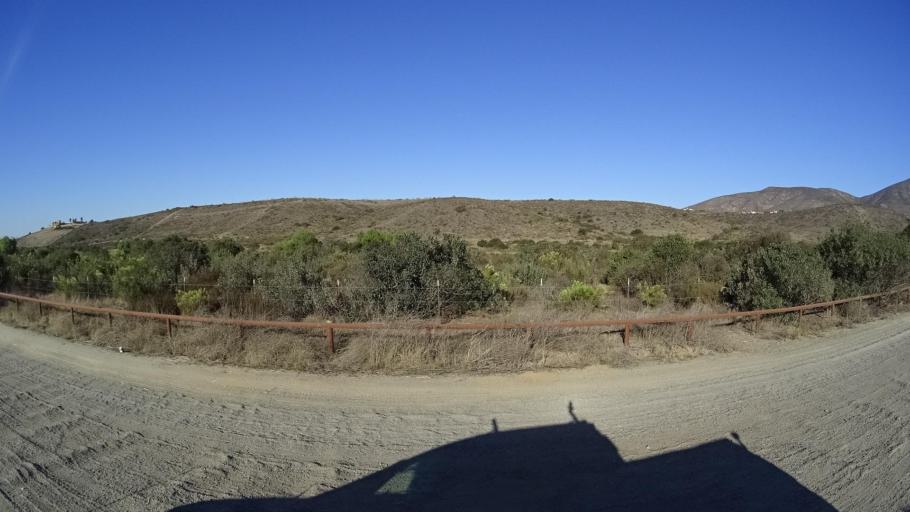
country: US
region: California
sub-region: San Diego County
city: Jamul
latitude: 32.6655
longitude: -116.9279
